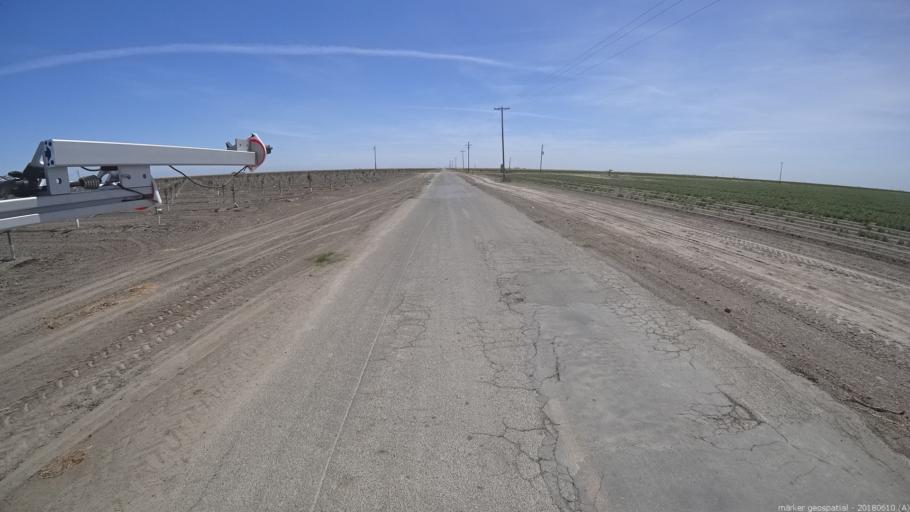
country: US
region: California
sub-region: Merced County
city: Dos Palos
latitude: 37.0546
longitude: -120.5122
